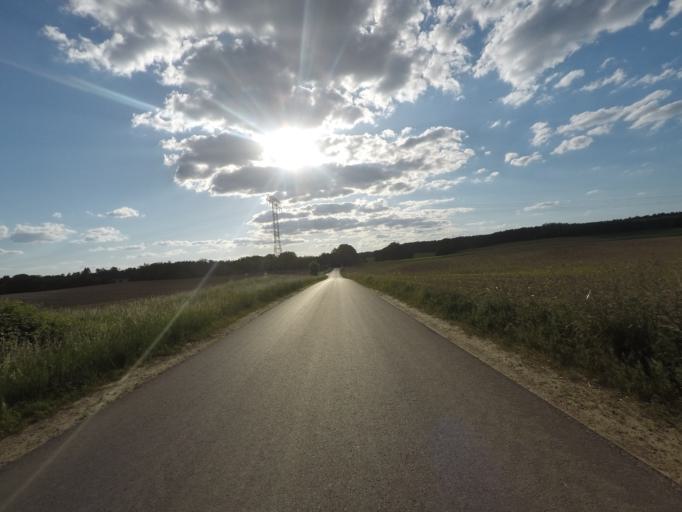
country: DE
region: Brandenburg
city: Britz
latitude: 52.8930
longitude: 13.7785
